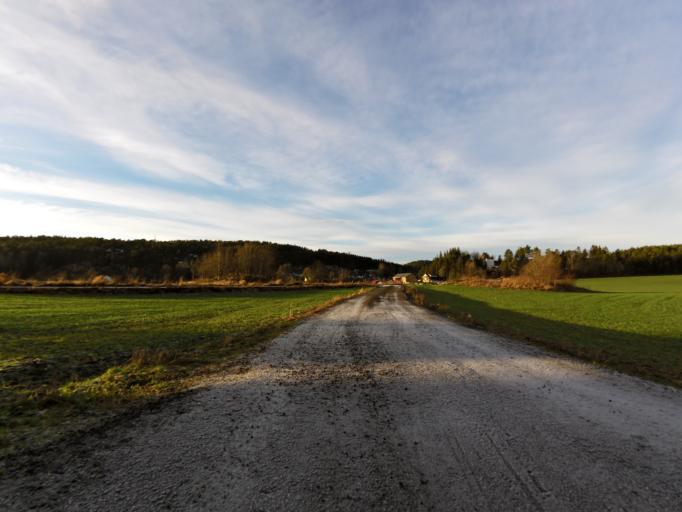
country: NO
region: Ostfold
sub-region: Fredrikstad
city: Fredrikstad
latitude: 59.2418
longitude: 10.9057
